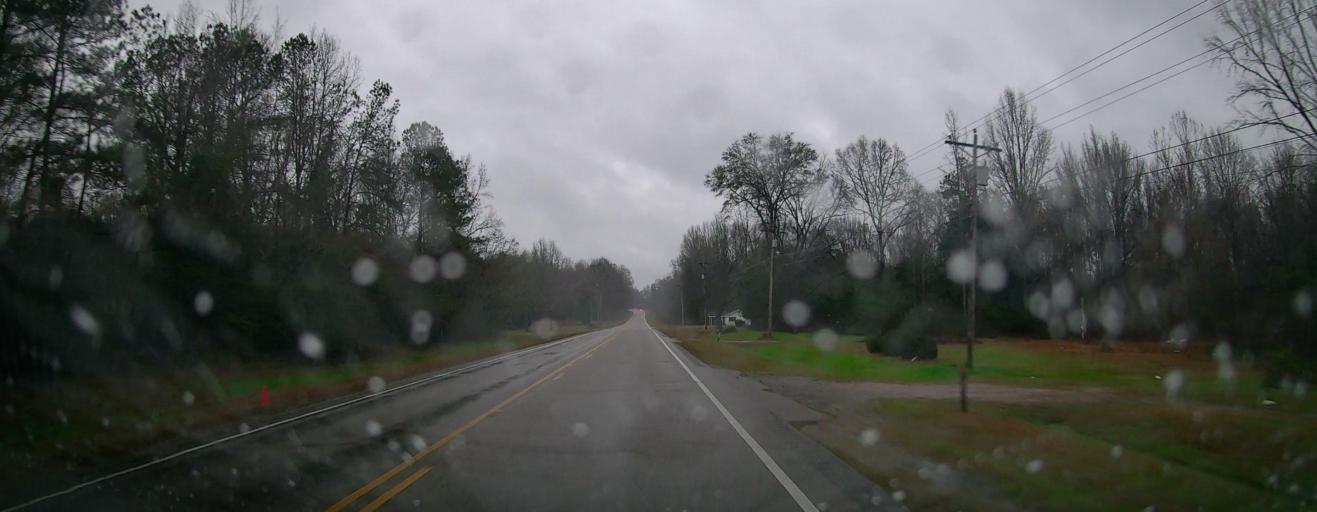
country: US
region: Alabama
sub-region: Autauga County
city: Prattville
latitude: 32.5054
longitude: -86.5858
